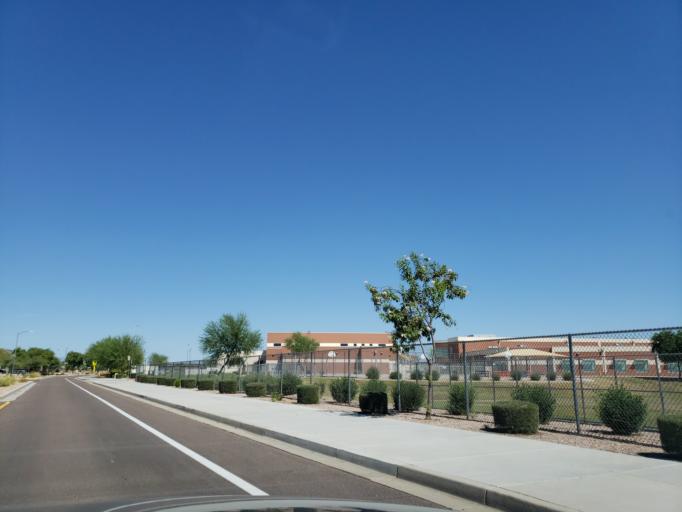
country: US
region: Arizona
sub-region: Maricopa County
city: Sun City West
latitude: 33.6778
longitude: -112.2704
